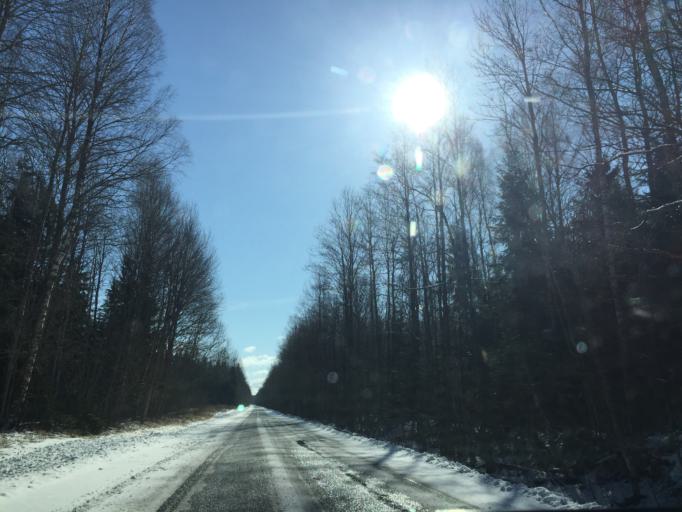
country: LV
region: Salacgrivas
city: Ainazi
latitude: 58.0043
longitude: 24.5102
